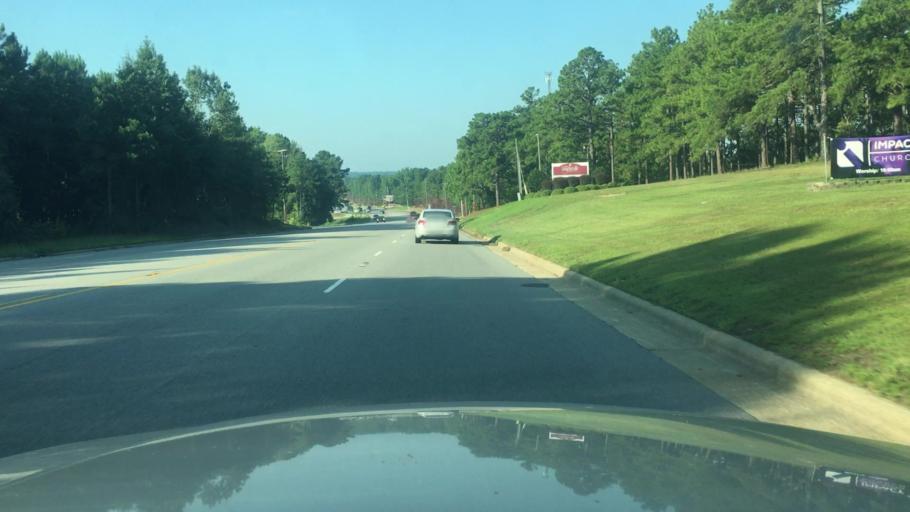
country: US
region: North Carolina
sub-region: Cumberland County
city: Eastover
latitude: 35.1791
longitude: -78.8565
